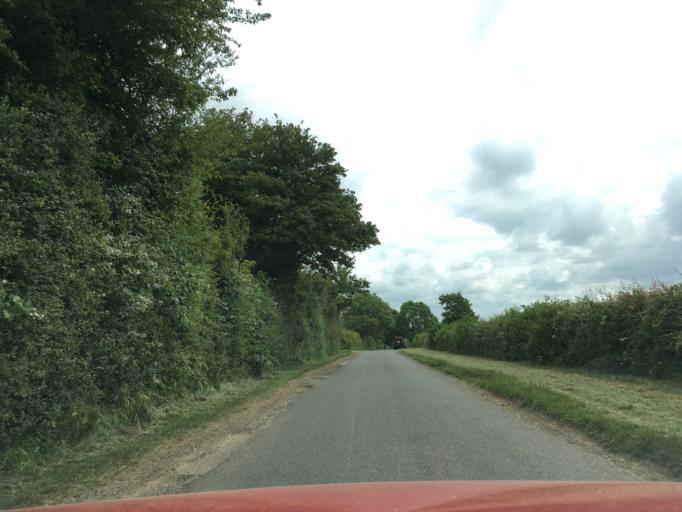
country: GB
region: England
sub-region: Oxfordshire
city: Chipping Norton
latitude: 51.9214
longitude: -1.5189
